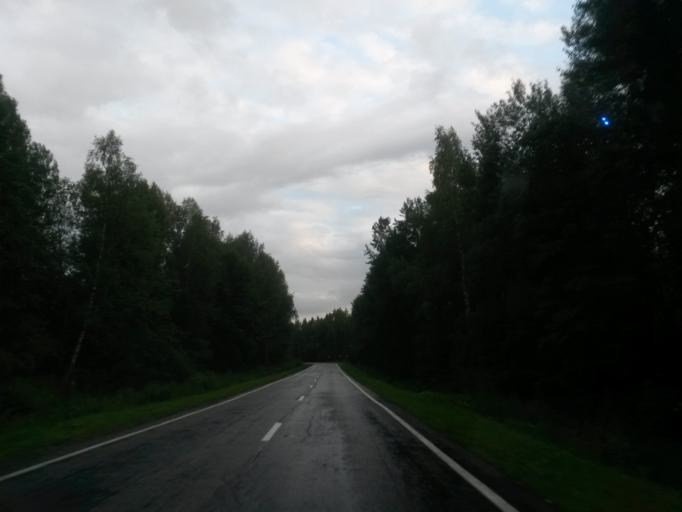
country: RU
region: Jaroslavl
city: Tutayev
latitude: 57.9156
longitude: 39.5154
